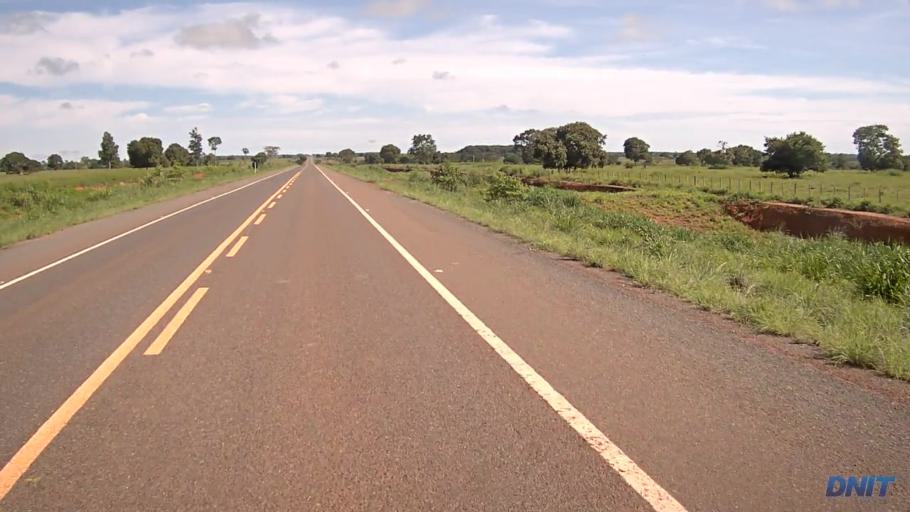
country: BR
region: Goias
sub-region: Sao Miguel Do Araguaia
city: Sao Miguel do Araguaia
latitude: -13.3888
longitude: -50.1385
